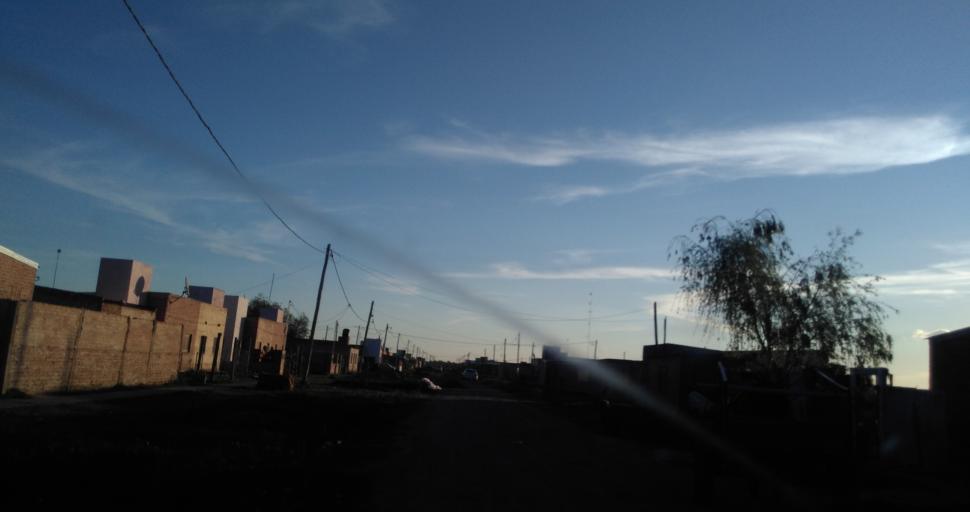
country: AR
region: Chaco
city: Resistencia
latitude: -27.4700
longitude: -59.0226
